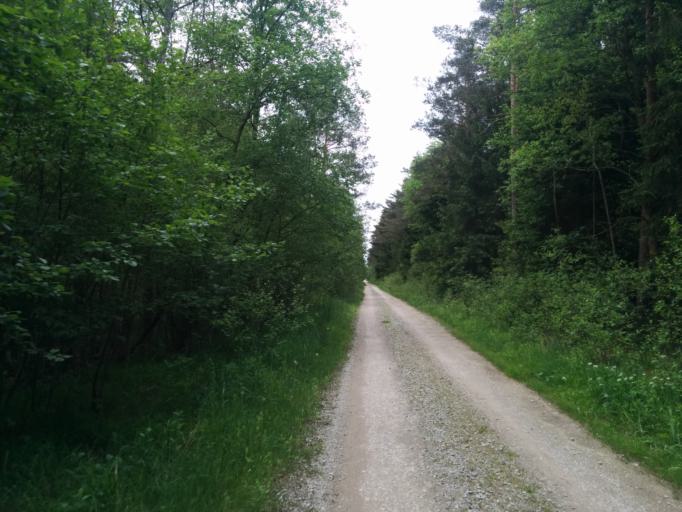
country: DE
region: Bavaria
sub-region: Regierungsbezirk Mittelfranken
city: Buckenhof
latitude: 49.5523
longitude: 11.0477
